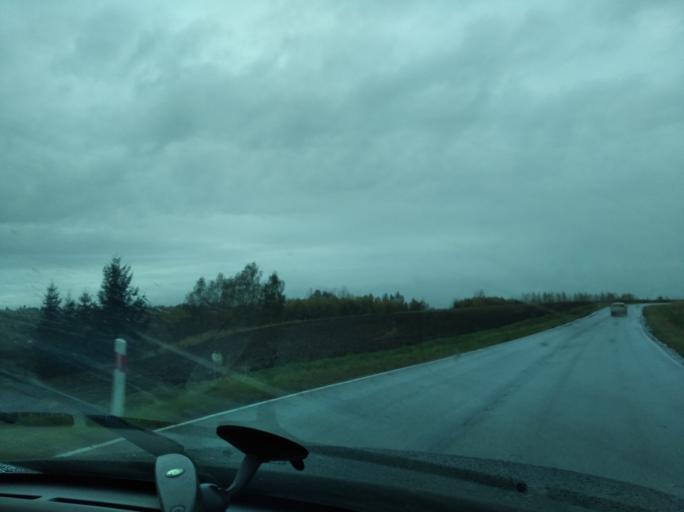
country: PL
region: Subcarpathian Voivodeship
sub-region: Powiat lancucki
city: Handzlowka
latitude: 50.0000
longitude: 22.1987
